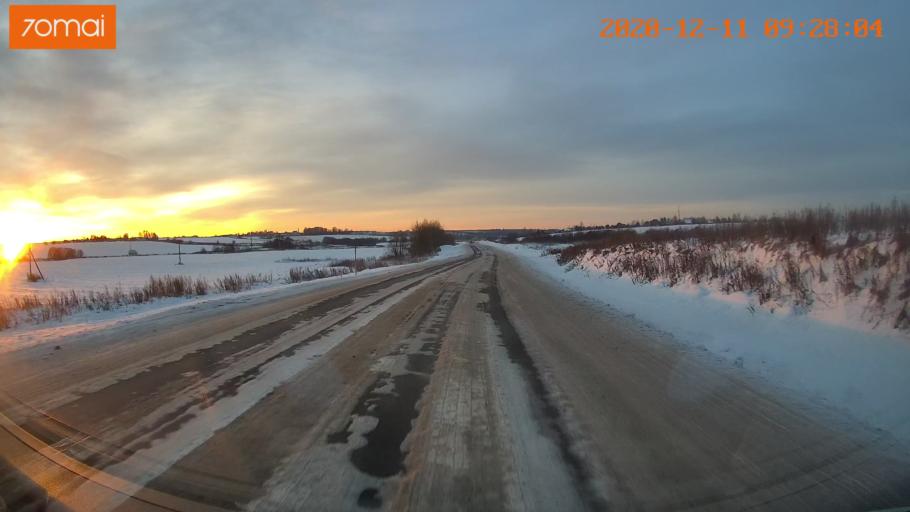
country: RU
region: Vologda
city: Vologda
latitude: 59.1574
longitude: 40.0102
